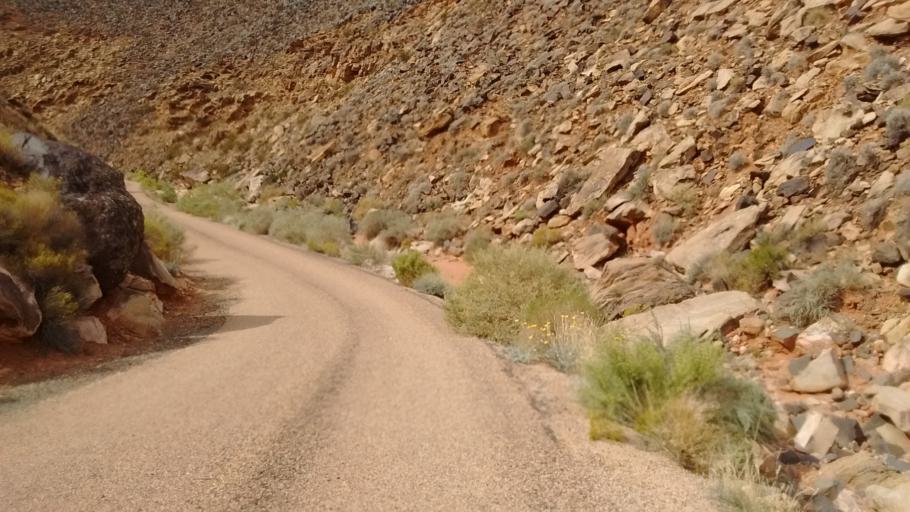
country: US
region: Utah
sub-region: Washington County
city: Washington
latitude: 37.1278
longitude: -113.4766
